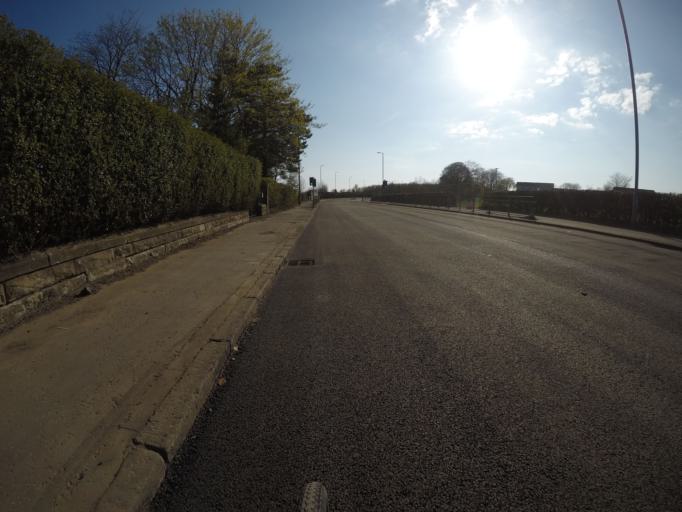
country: GB
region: Scotland
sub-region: North Ayrshire
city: Kilwinning
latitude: 55.6515
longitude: -4.7188
